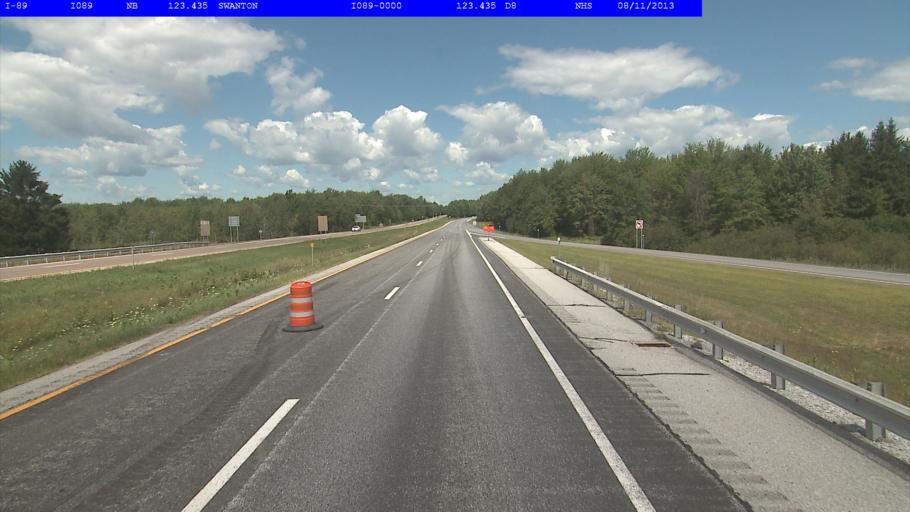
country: US
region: Vermont
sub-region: Franklin County
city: Swanton
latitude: 44.9232
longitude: -73.1079
